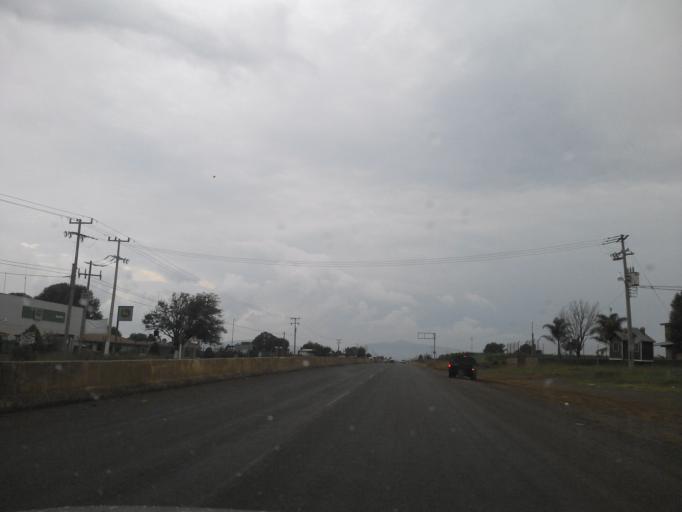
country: MX
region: Jalisco
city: Arandas
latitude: 20.7187
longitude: -102.4426
